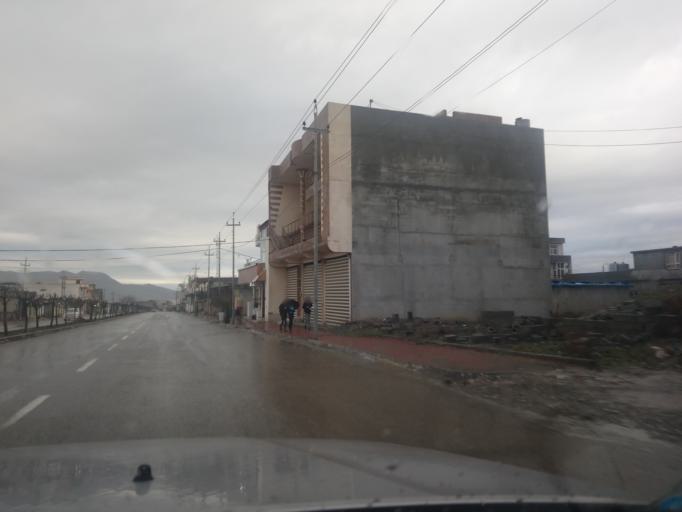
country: IQ
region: As Sulaymaniyah
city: Qeladize
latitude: 36.1776
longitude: 45.1491
